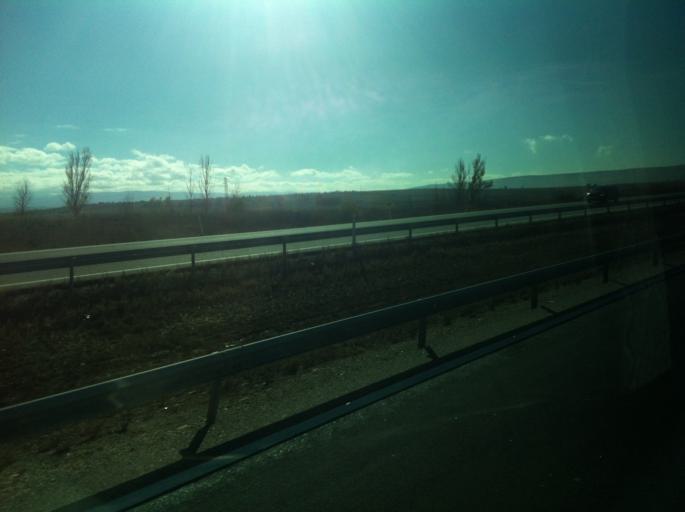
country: ES
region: Castille and Leon
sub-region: Provincia de Burgos
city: Fresno de Rodilla
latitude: 42.4289
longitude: -3.5014
